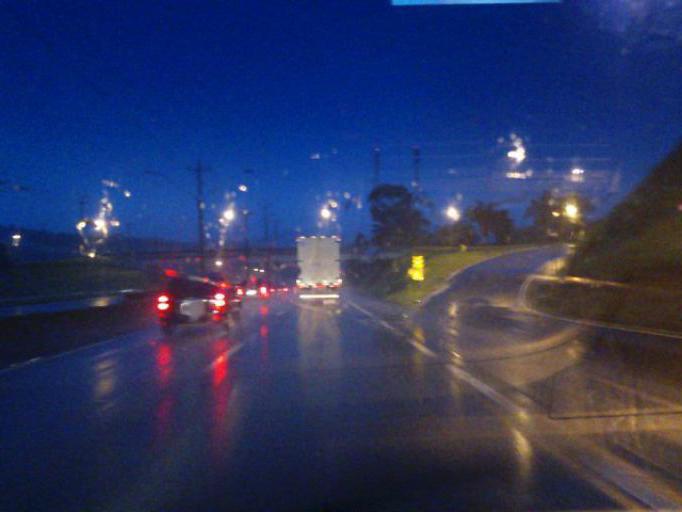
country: BR
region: Sao Paulo
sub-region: Juquitiba
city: Juquitiba
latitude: -23.9260
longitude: -46.9941
